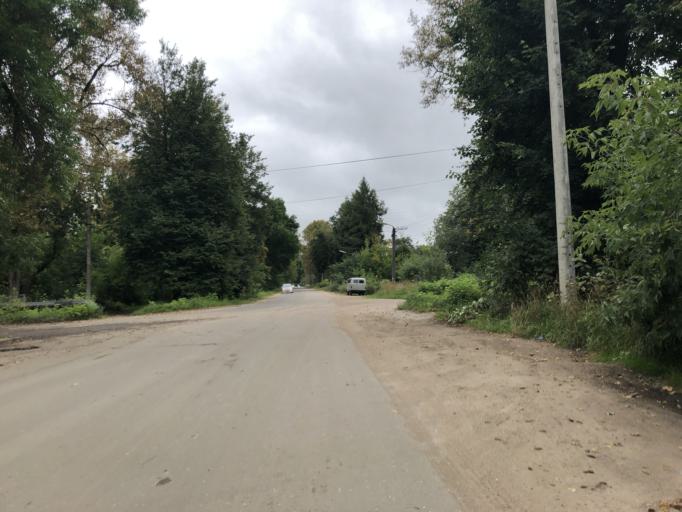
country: RU
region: Tverskaya
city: Rzhev
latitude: 56.2433
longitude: 34.3301
